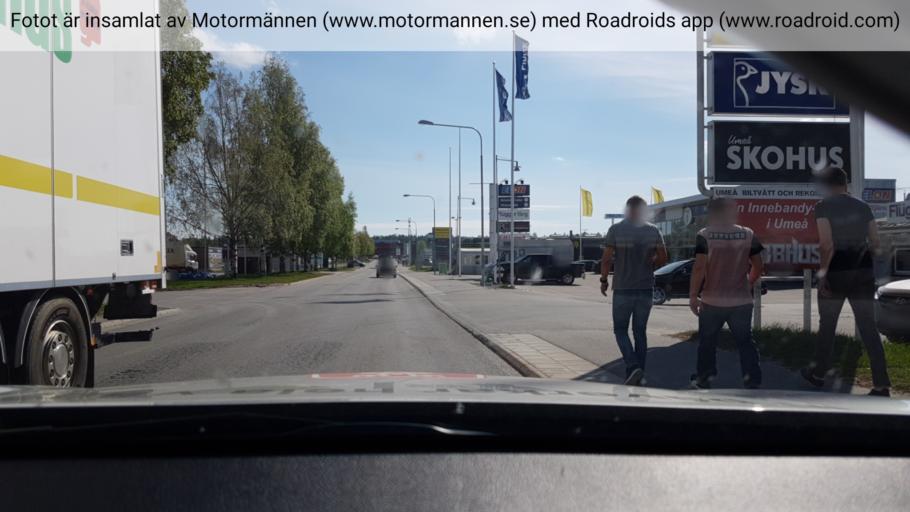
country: SE
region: Vaesterbotten
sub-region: Umea Kommun
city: Ersmark
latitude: 63.8510
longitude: 20.3069
